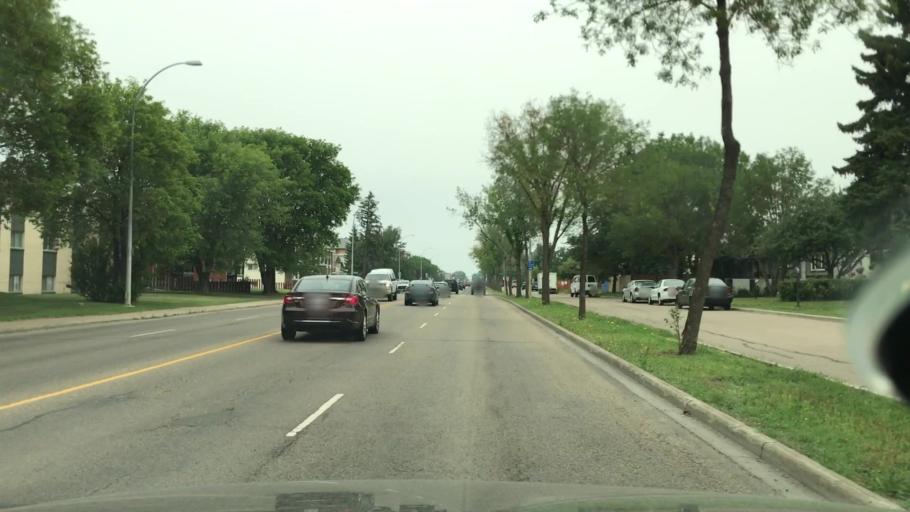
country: CA
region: Alberta
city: Edmonton
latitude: 53.5351
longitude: -113.5779
